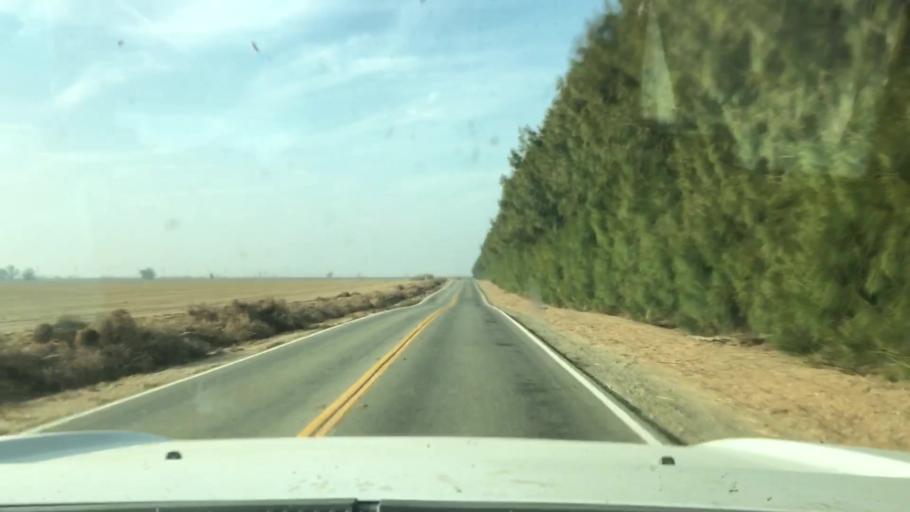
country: US
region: California
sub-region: Kern County
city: Lost Hills
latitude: 35.5033
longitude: -119.7425
